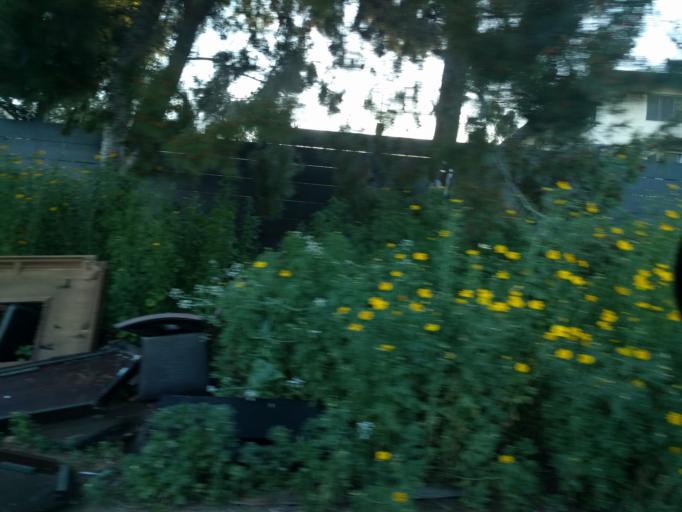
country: US
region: California
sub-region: San Diego County
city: San Diego
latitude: 32.7164
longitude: -117.1253
